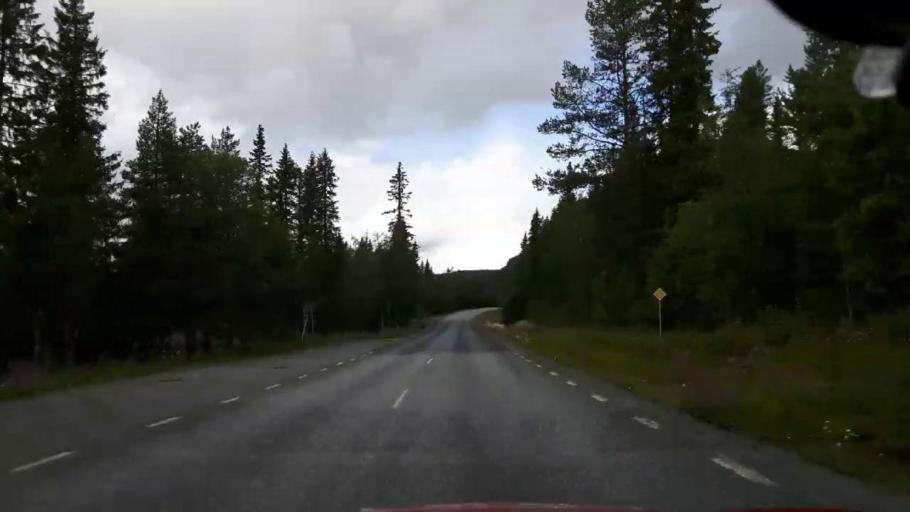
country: SE
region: Vaesterbotten
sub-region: Vilhelmina Kommun
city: Sjoberg
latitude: 64.9418
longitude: 15.8366
